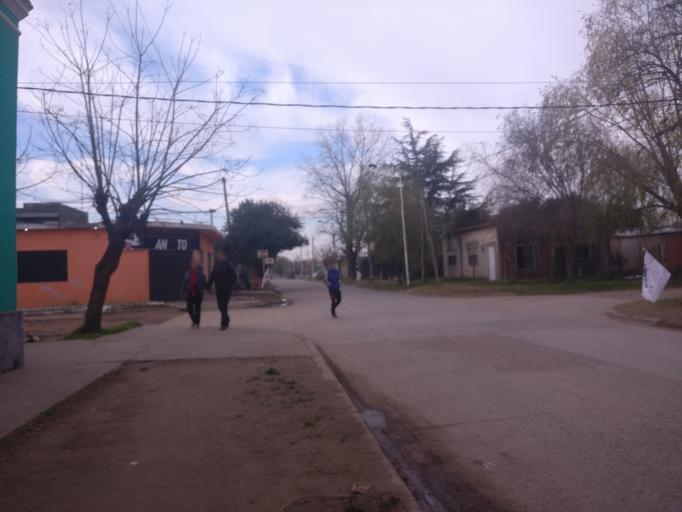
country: AR
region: Buenos Aires
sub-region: Partido de Ezeiza
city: Ezeiza
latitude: -34.9407
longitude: -58.6124
